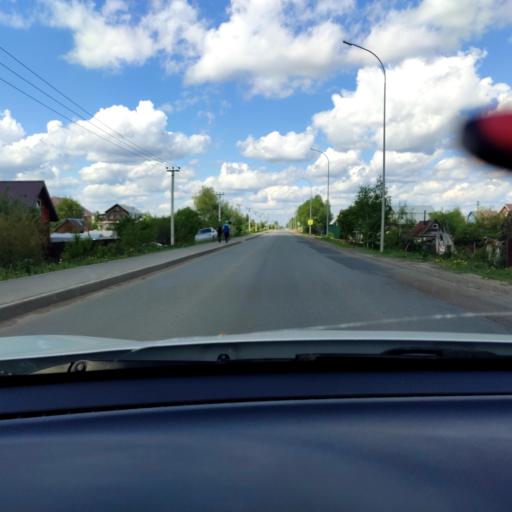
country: RU
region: Tatarstan
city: Stolbishchi
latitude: 55.6948
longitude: 49.1994
